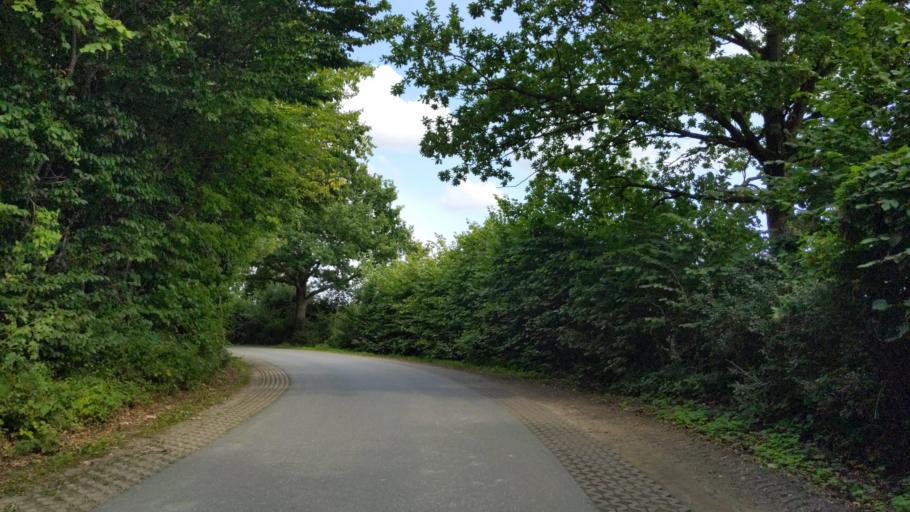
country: DE
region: Schleswig-Holstein
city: Neustadt in Holstein
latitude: 54.1391
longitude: 10.7942
